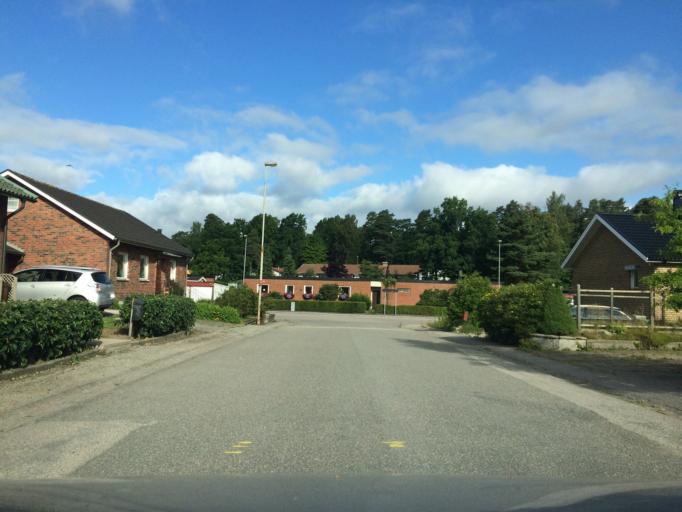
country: SE
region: Vaestra Goetaland
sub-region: Trollhattan
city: Trollhattan
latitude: 58.2909
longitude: 12.3250
